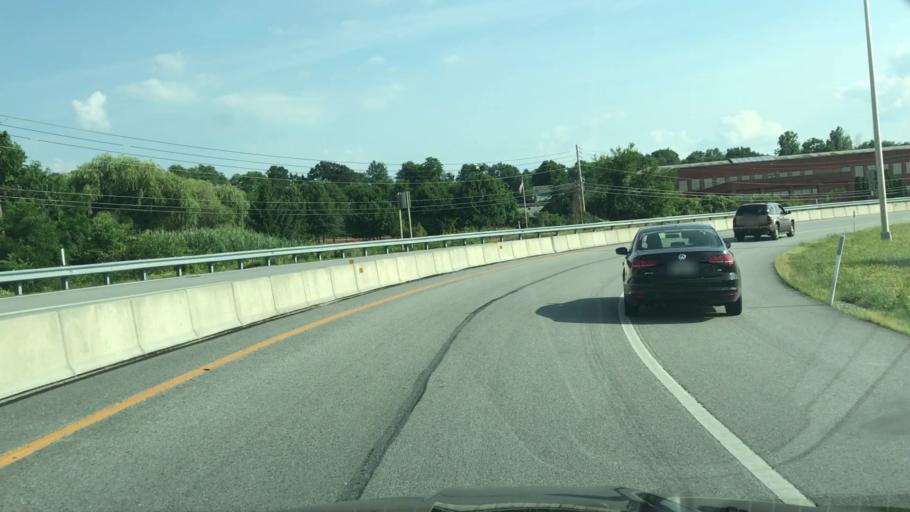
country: US
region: Pennsylvania
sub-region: Cumberland County
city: Shiremanstown
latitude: 40.1983
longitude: -76.9711
